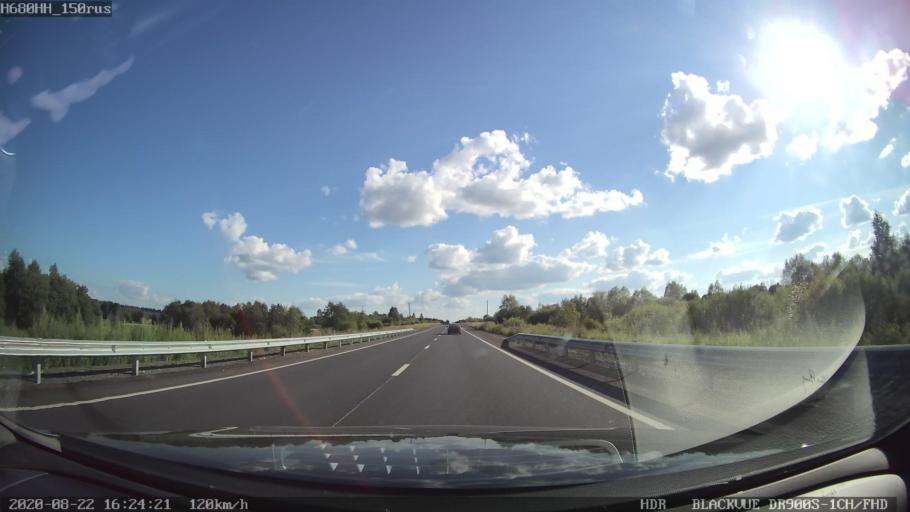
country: RU
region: Tverskaya
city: Rameshki
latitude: 57.3388
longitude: 36.0960
